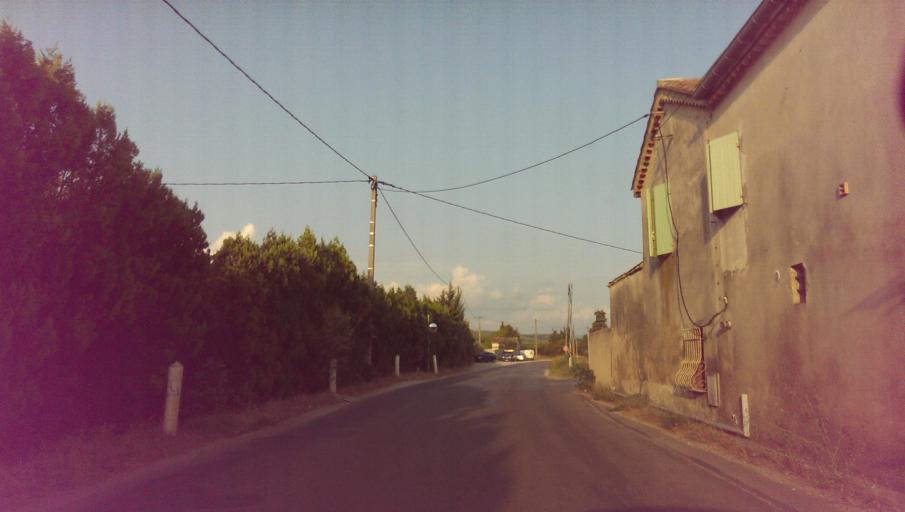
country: FR
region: Provence-Alpes-Cote d'Azur
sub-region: Departement du Vaucluse
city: Carpentras
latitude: 44.0316
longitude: 5.0586
